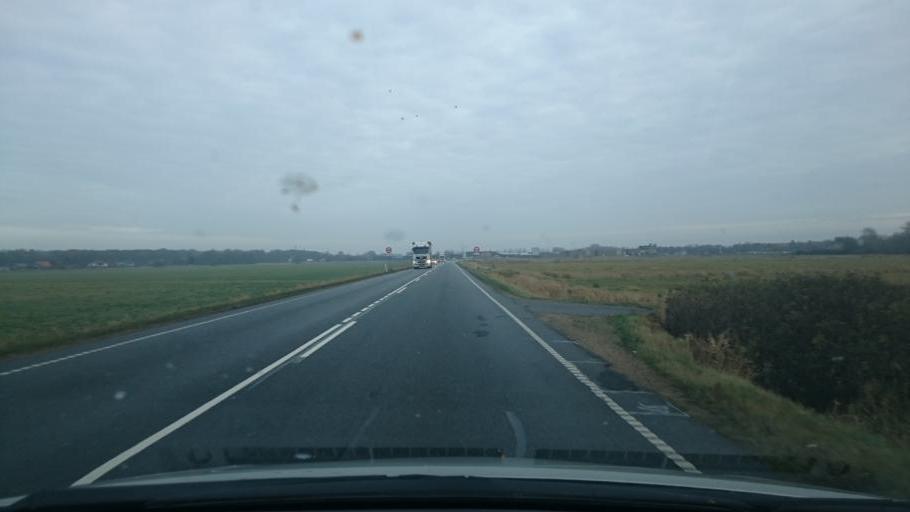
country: DK
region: South Denmark
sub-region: Esbjerg Kommune
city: Ribe
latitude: 55.3343
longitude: 8.7586
